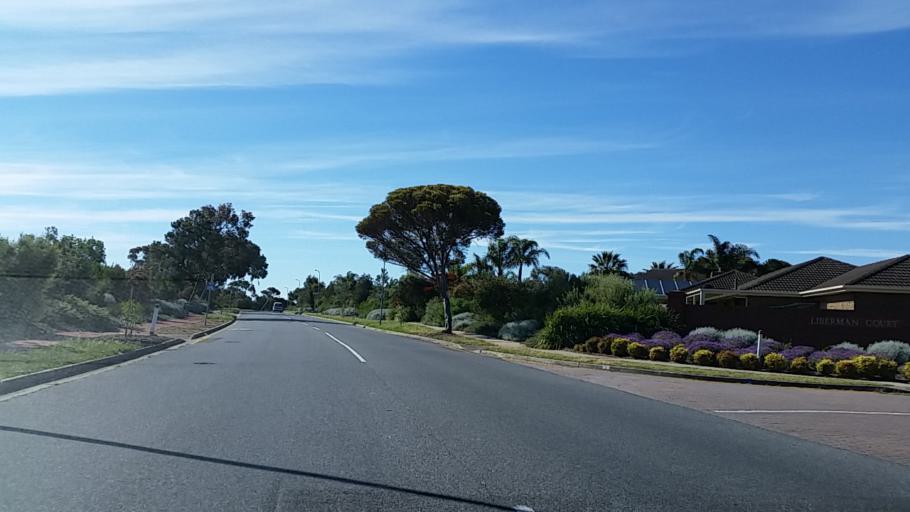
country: AU
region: South Australia
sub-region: Charles Sturt
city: West Lakes Shore
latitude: -34.8704
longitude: 138.4918
